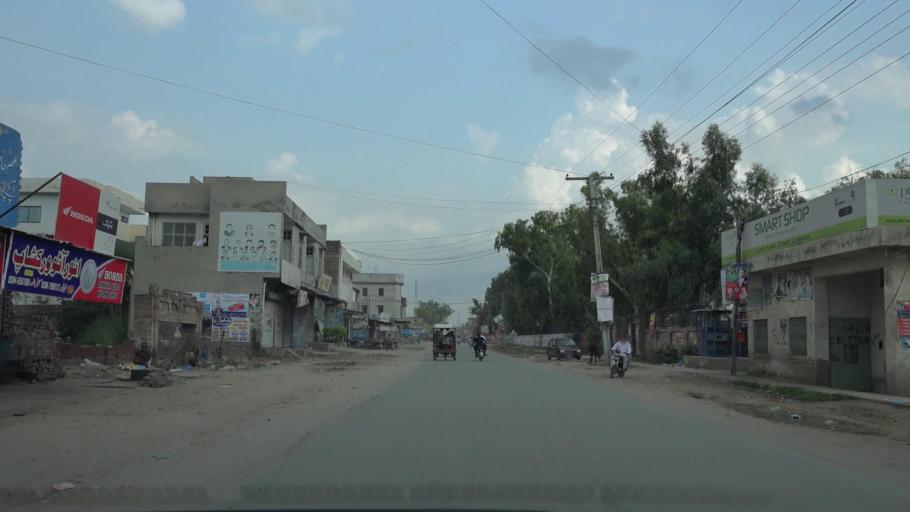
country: PK
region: Punjab
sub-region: Nankana Sahib District
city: Shahkot
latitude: 31.5746
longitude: 73.4838
